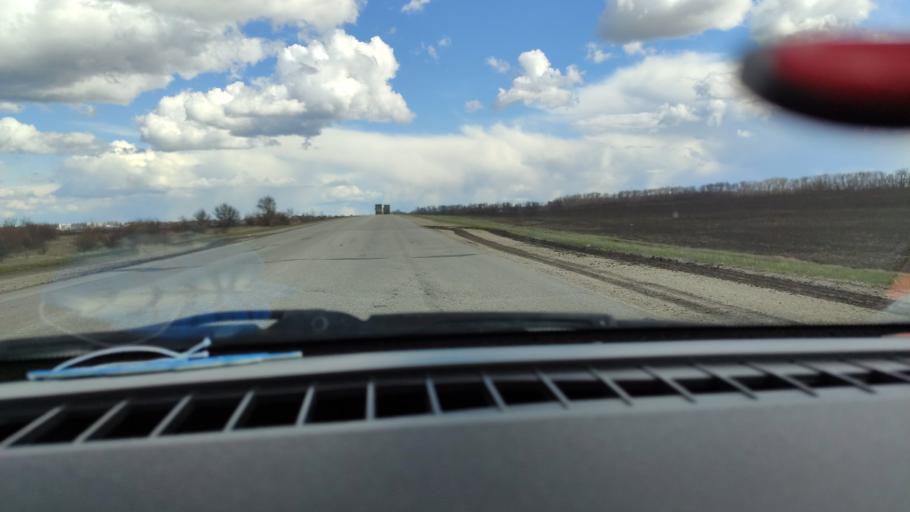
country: RU
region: Samara
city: Varlamovo
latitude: 53.1186
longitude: 48.3369
